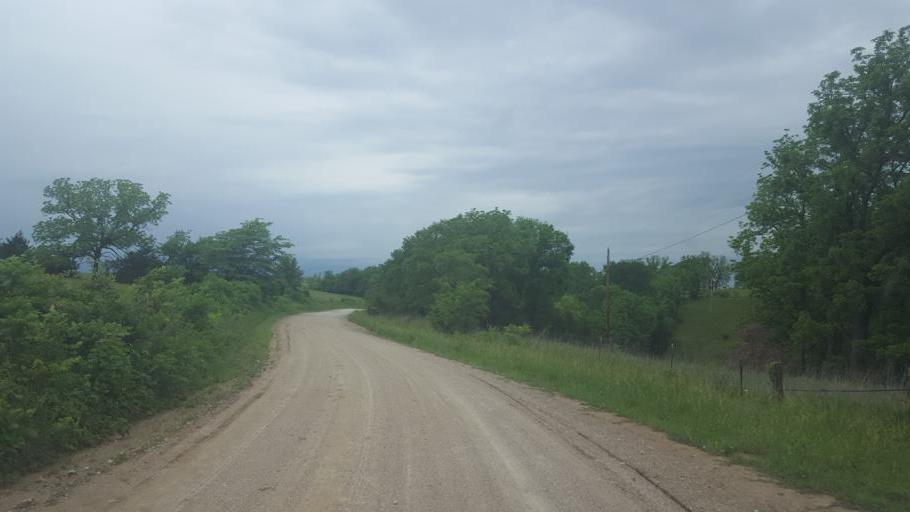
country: US
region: Missouri
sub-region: Moniteau County
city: California
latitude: 38.7563
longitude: -92.6056
